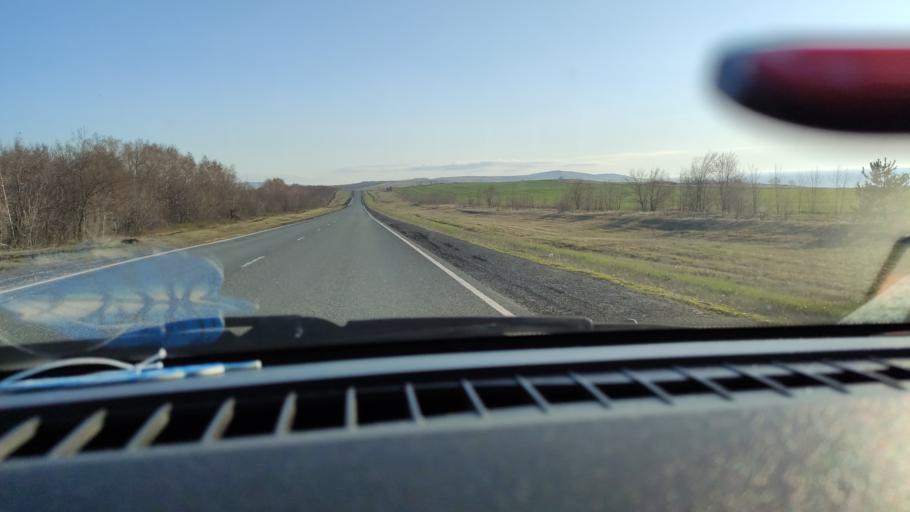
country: RU
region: Saratov
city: Balakovo
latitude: 52.1859
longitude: 47.8479
